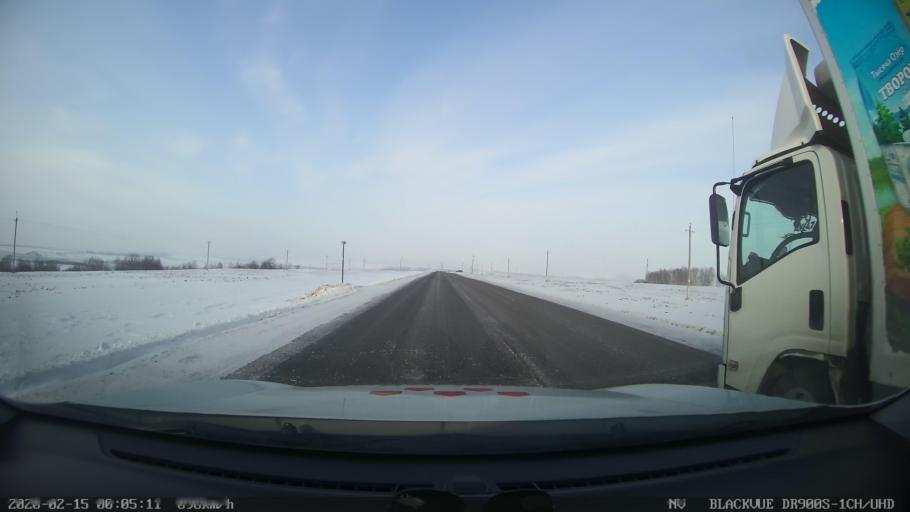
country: RU
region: Tatarstan
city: Kuybyshevskiy Zaton
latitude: 55.3929
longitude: 48.9792
